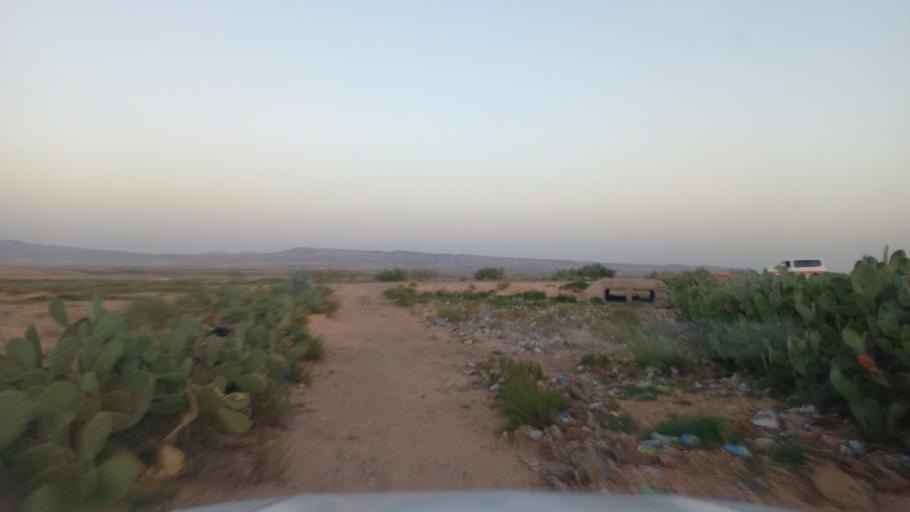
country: TN
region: Al Qasrayn
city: Sbiba
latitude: 35.3750
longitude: 9.0148
